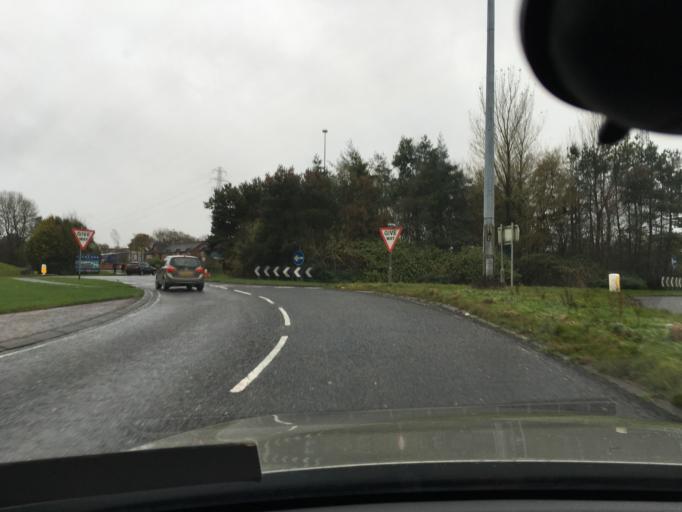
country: GB
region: Northern Ireland
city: Carnmoney
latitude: 54.6931
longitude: -5.9703
